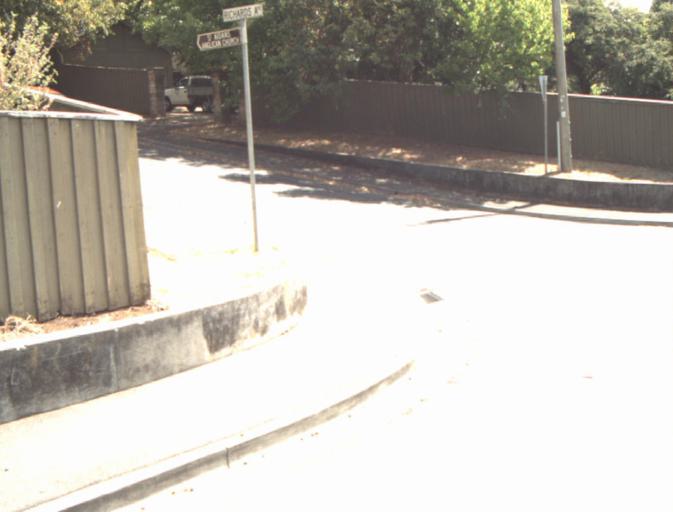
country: AU
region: Tasmania
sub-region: Launceston
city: East Launceston
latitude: -41.4376
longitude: 147.1579
